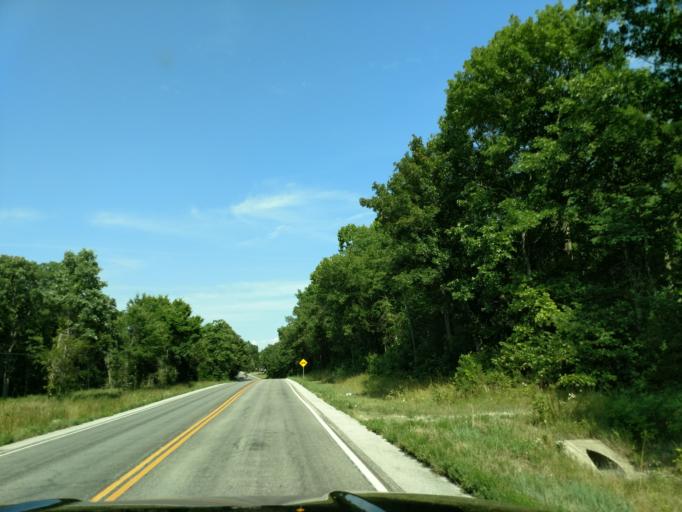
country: US
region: Missouri
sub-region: Barry County
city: Shell Knob
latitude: 36.6097
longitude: -93.5845
